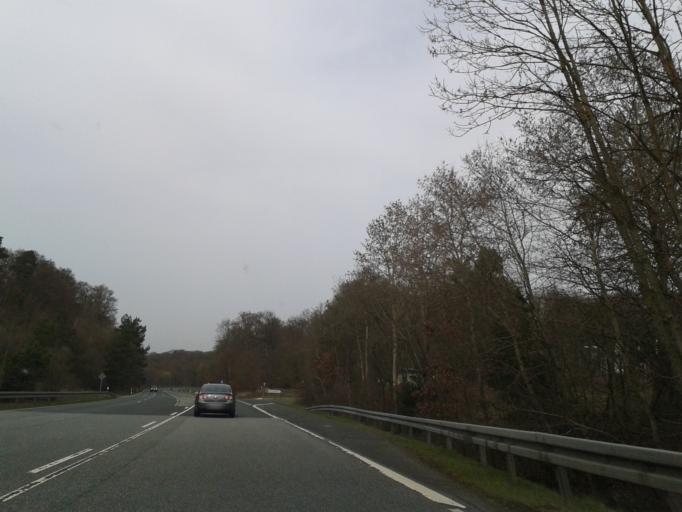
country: DE
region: Hesse
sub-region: Regierungsbezirk Giessen
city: Breitscheid
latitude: 50.6672
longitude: 8.2395
